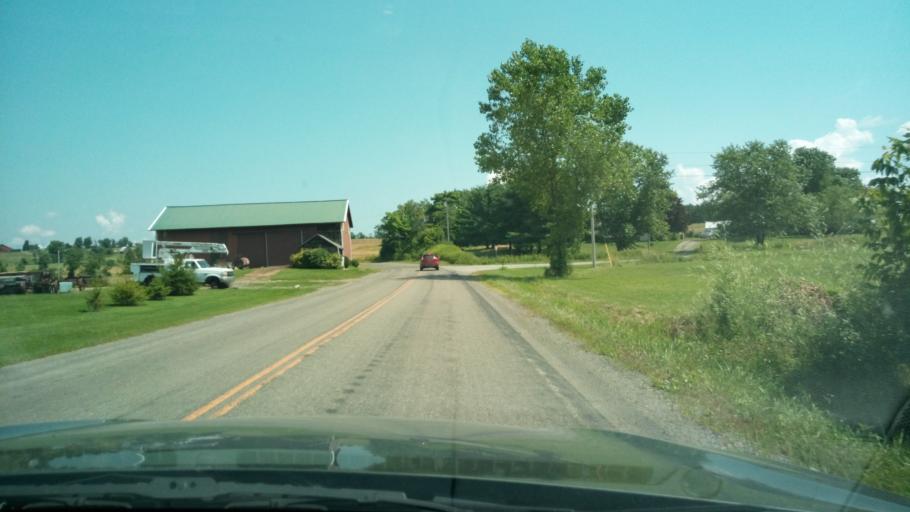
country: US
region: New York
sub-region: Chemung County
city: Horseheads North
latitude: 42.2751
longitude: -76.7949
